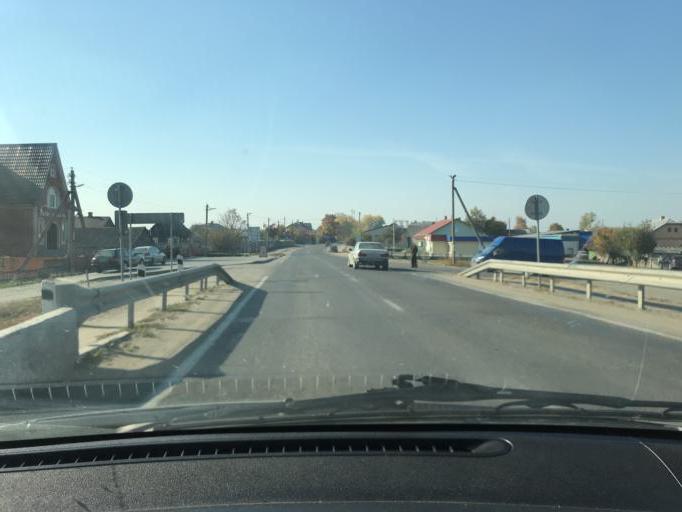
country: BY
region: Brest
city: Davyd-Haradok
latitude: 52.0767
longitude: 27.3444
